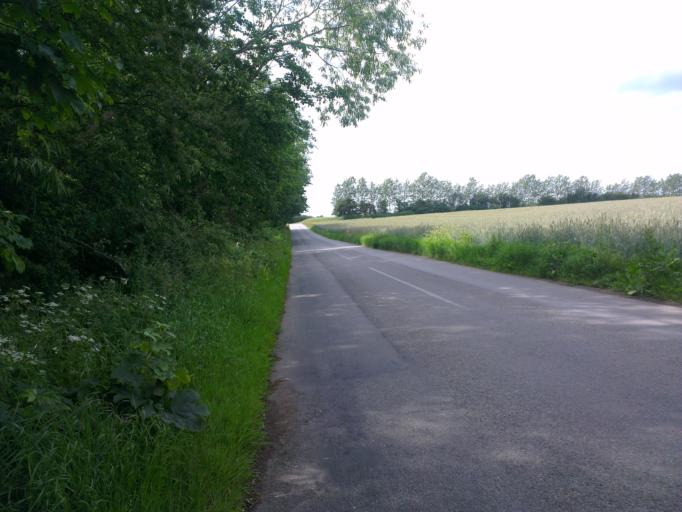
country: DK
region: Capital Region
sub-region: Frederikssund Kommune
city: Skibby
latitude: 55.7237
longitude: 11.9667
